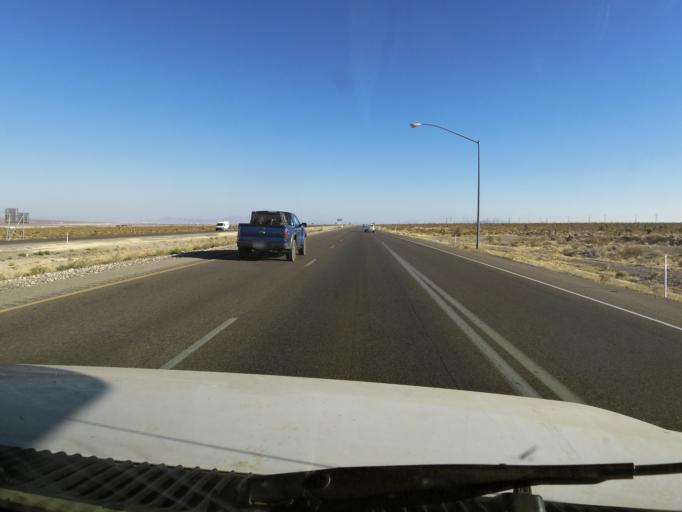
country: US
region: Nevada
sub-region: Clark County
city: Summerlin South
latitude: 36.3588
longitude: -115.3476
